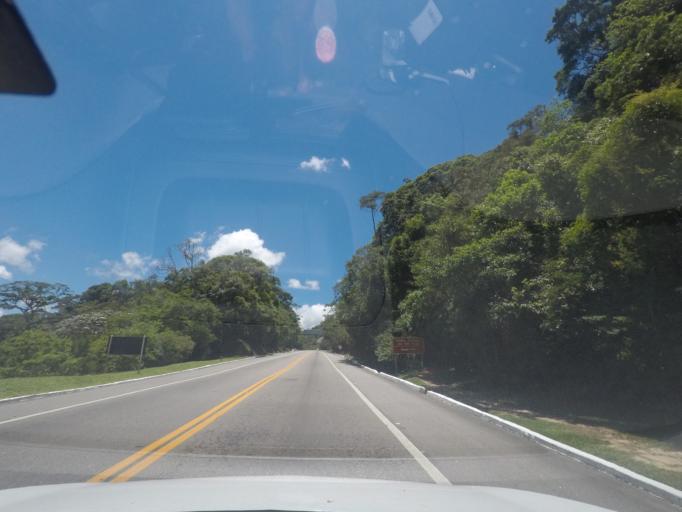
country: BR
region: Rio de Janeiro
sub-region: Teresopolis
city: Teresopolis
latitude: -22.4619
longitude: -42.9845
